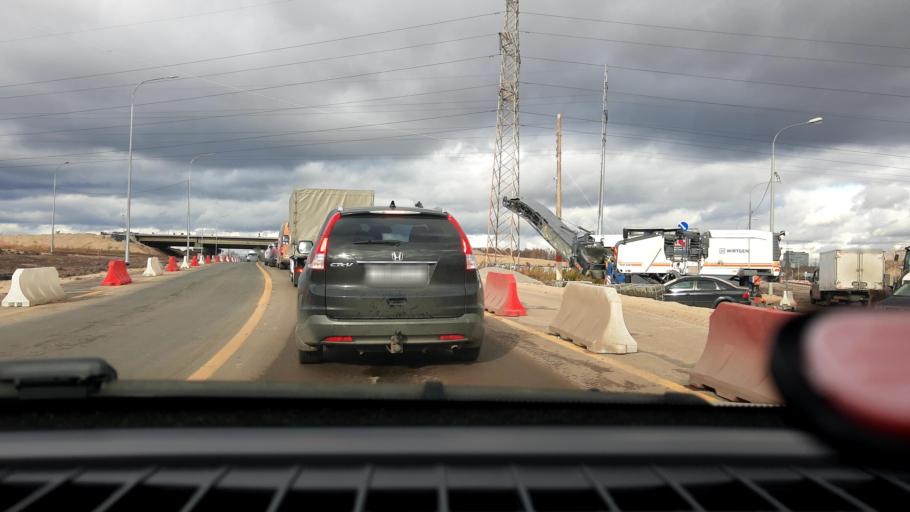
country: RU
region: Nizjnij Novgorod
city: Nizhniy Novgorod
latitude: 56.2131
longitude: 43.9291
